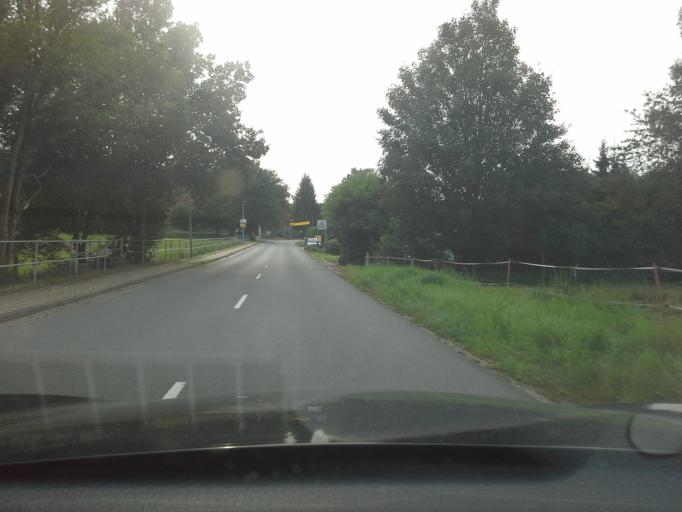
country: DE
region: Lower Saxony
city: Barsinghausen
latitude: 52.2586
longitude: 9.4473
